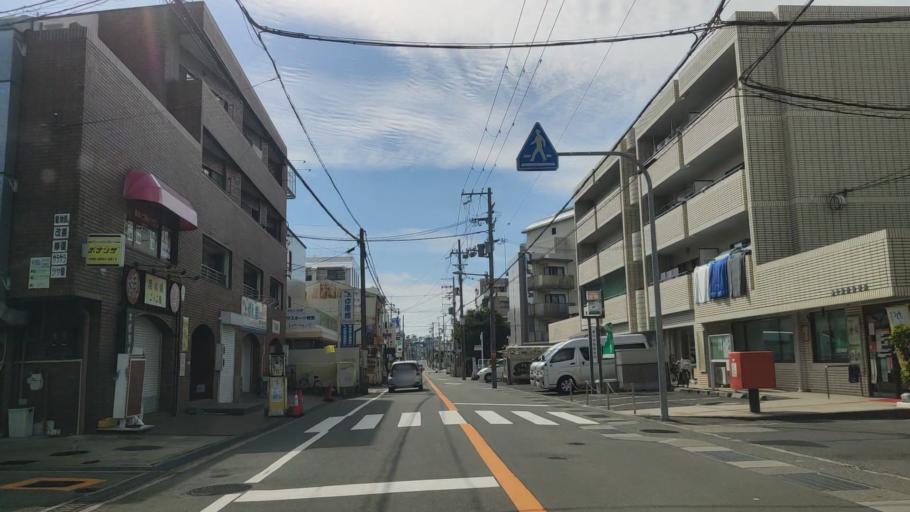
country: JP
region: Osaka
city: Toyonaka
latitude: 34.7970
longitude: 135.4641
